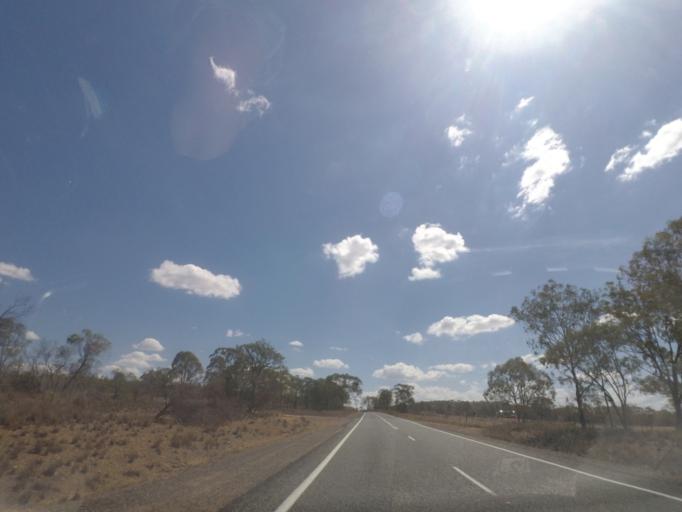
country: AU
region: Queensland
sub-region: Southern Downs
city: Warwick
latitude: -28.2183
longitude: 151.5589
